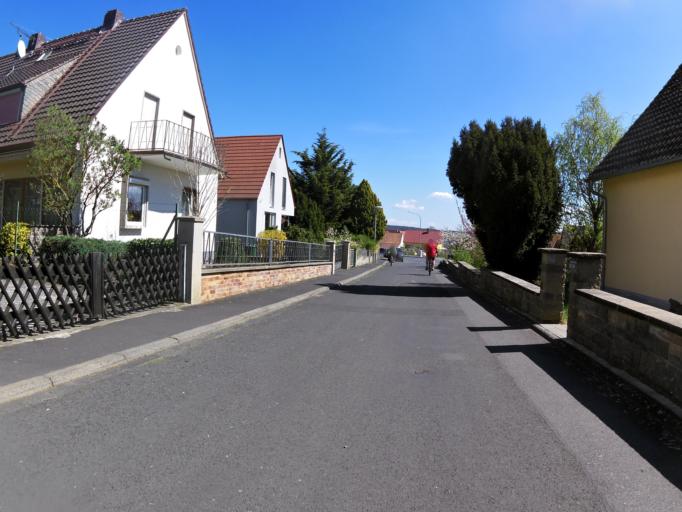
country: DE
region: Bavaria
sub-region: Regierungsbezirk Unterfranken
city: Volkach
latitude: 49.8623
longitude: 10.2131
